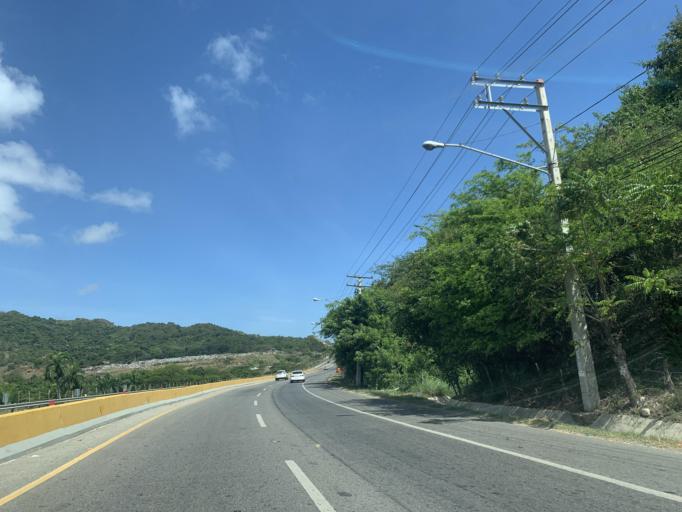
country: DO
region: Puerto Plata
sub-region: Puerto Plata
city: Puerto Plata
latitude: 19.8209
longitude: -70.7390
